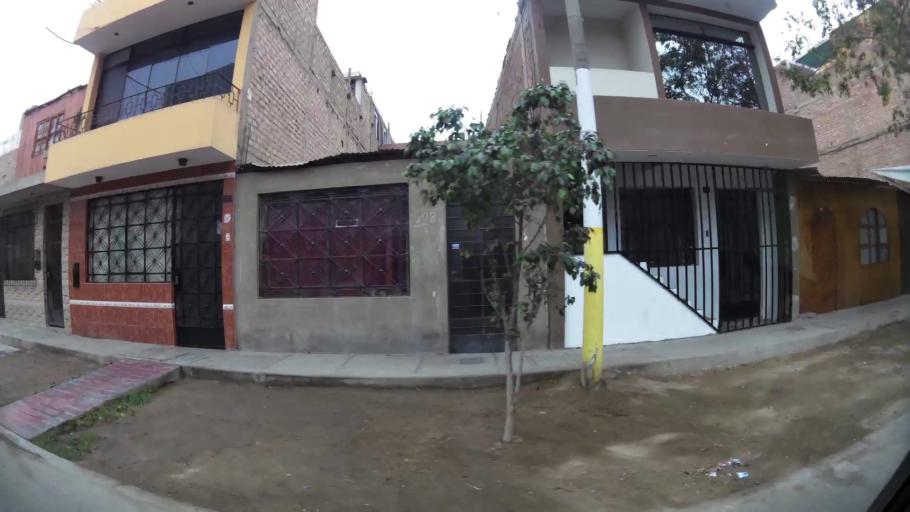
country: PE
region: Lima
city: Ventanilla
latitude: -11.8676
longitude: -77.0785
